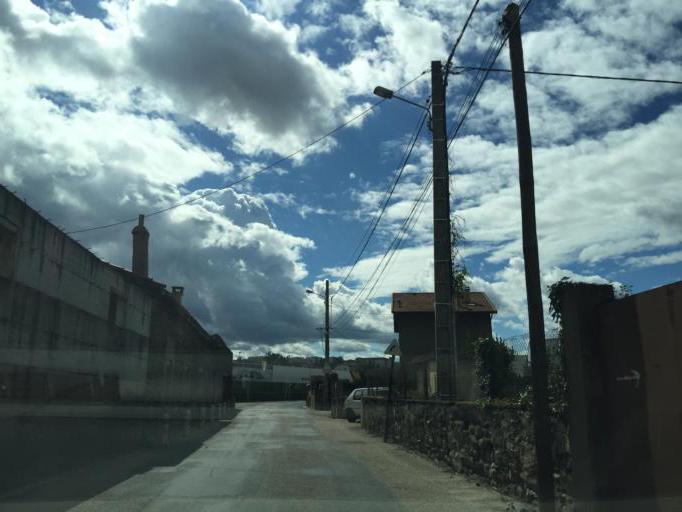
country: FR
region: Rhone-Alpes
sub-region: Departement de la Loire
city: Lorette
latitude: 45.5188
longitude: 4.5907
